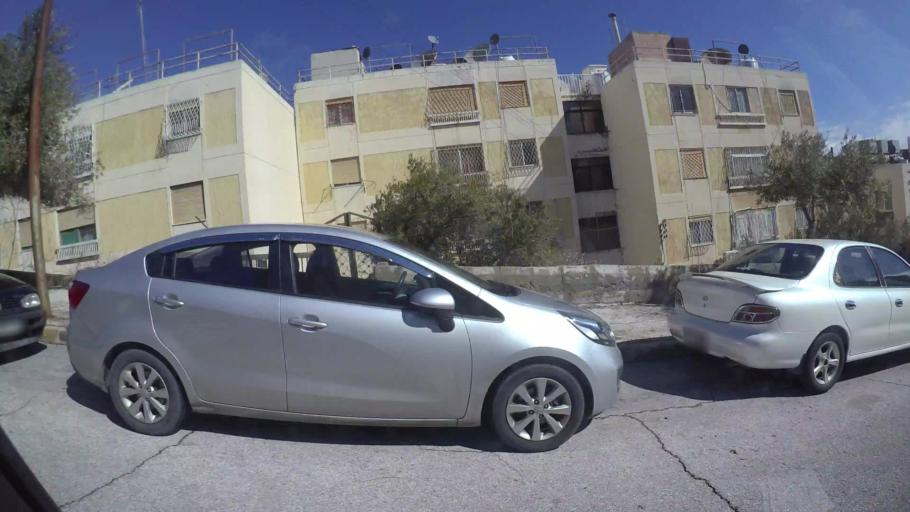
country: JO
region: Amman
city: Al Jubayhah
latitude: 32.0559
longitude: 35.8825
